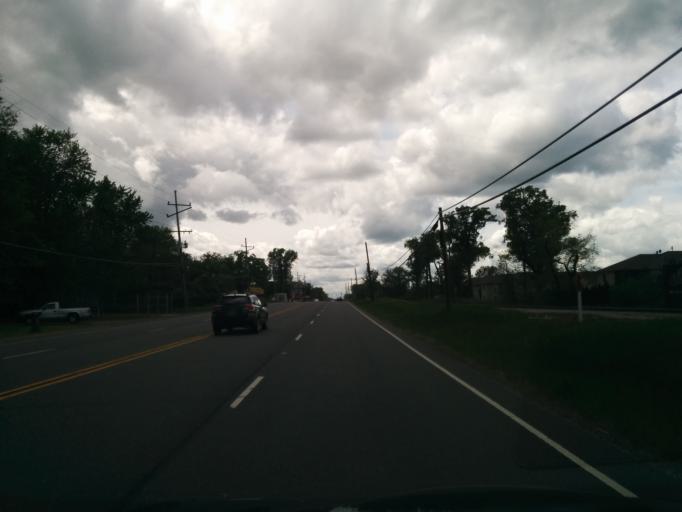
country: US
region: Indiana
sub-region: LaPorte County
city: Long Beach
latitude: 41.7354
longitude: -86.8514
